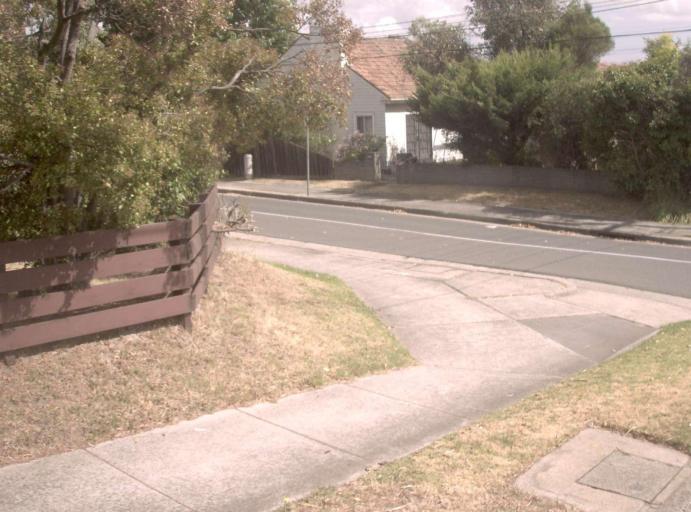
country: AU
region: Victoria
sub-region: Monash
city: Chadstone
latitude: -37.8885
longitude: 145.1078
